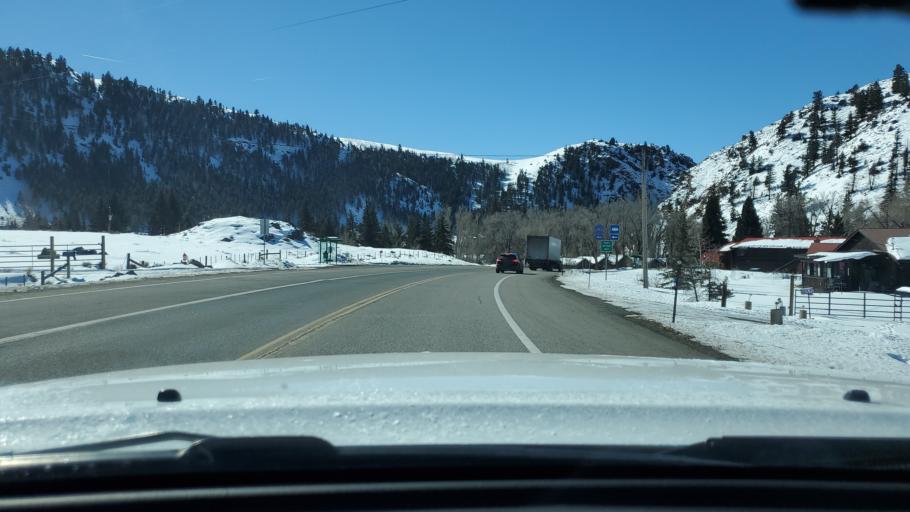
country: US
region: Colorado
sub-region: Gunnison County
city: Gunnison
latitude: 38.6662
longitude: -106.8459
